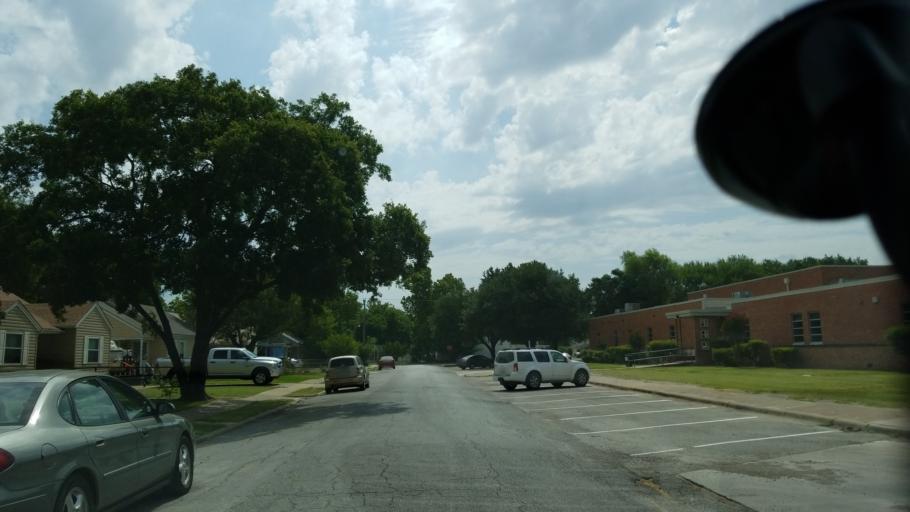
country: US
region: Texas
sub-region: Dallas County
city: Grand Prairie
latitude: 32.7525
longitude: -96.9874
